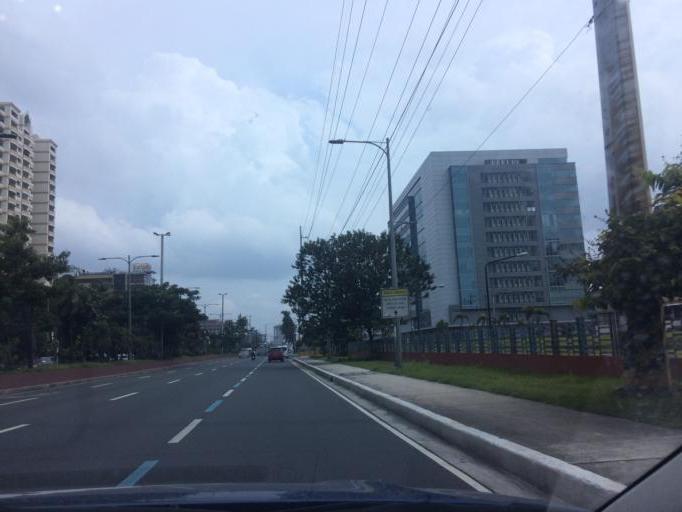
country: PH
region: Metro Manila
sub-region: Makati City
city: Makati City
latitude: 14.5422
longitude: 120.9917
